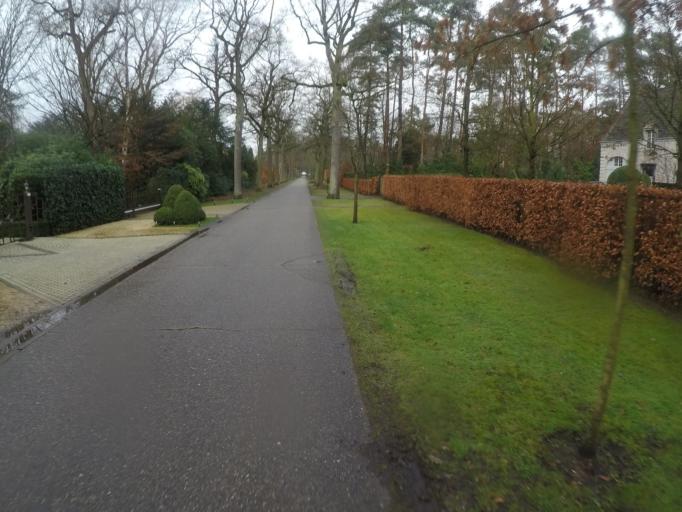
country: BE
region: Flanders
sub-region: Provincie Antwerpen
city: Schilde
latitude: 51.2291
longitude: 4.5662
